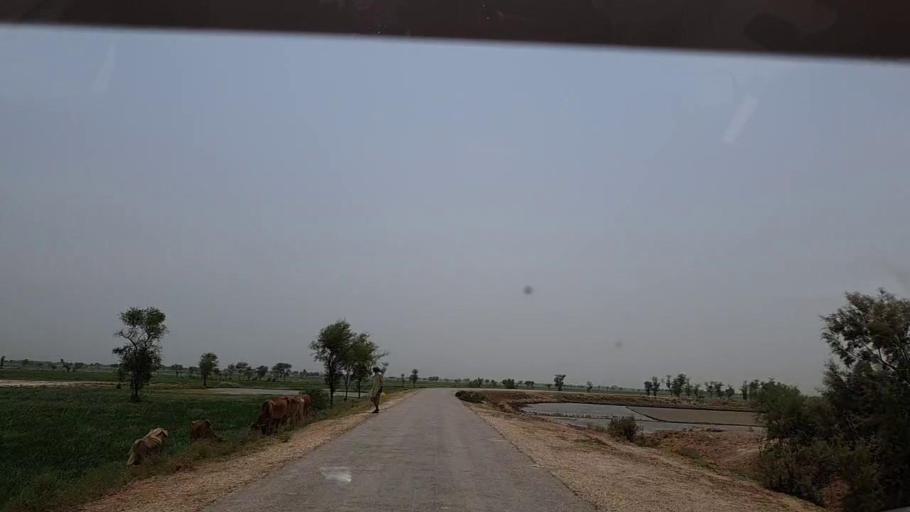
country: PK
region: Sindh
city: Khairpur Nathan Shah
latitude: 27.0202
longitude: 67.6652
